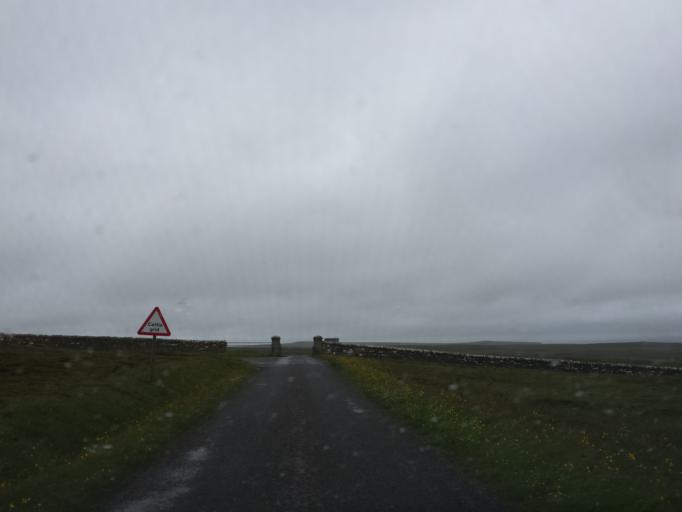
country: GB
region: Scotland
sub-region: Highland
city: Thurso
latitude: 58.6699
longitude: -3.3767
